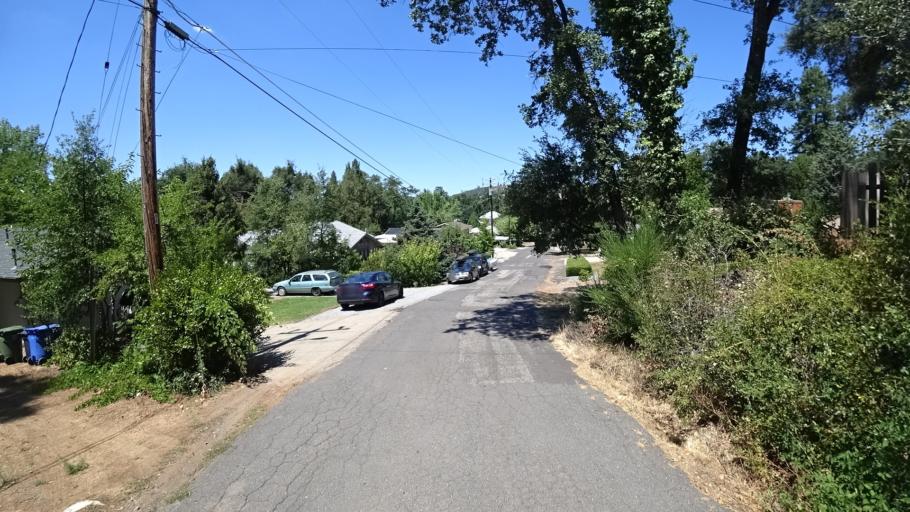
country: US
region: California
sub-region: Calaveras County
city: Murphys
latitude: 38.1357
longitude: -120.4540
